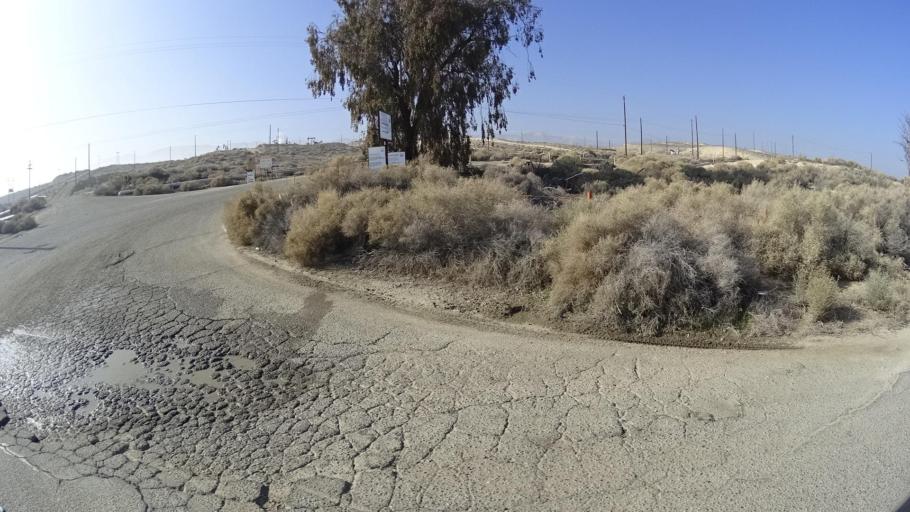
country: US
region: California
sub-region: Kern County
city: Taft Heights
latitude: 35.1595
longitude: -119.5236
